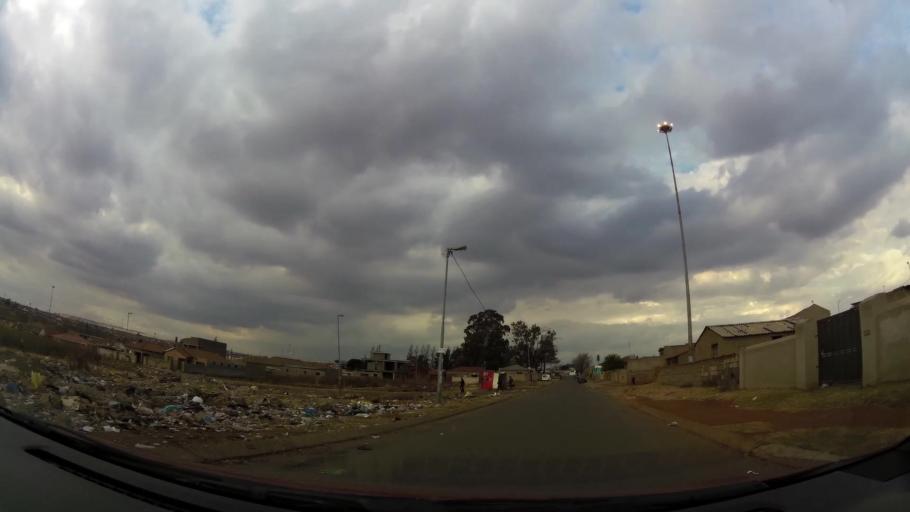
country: ZA
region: Gauteng
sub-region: City of Johannesburg Metropolitan Municipality
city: Soweto
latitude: -26.2412
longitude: 27.8158
